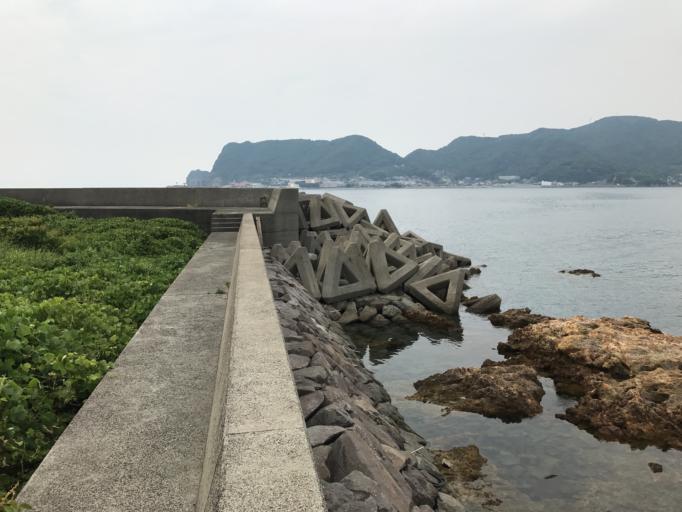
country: JP
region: Nagasaki
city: Nagasaki-shi
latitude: 32.7323
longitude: 129.8275
